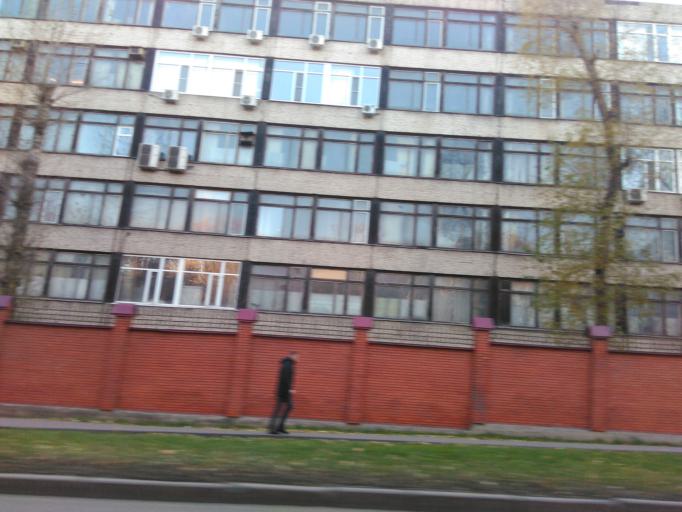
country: RU
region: Moscow
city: Ostankinskiy
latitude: 55.8315
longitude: 37.5993
